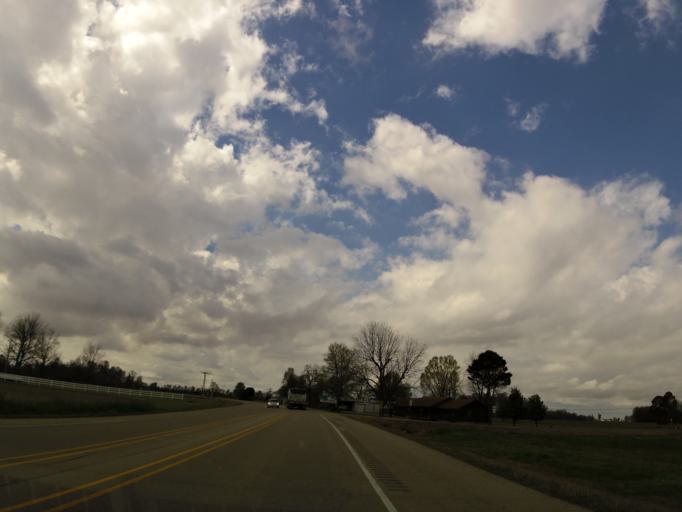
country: US
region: Arkansas
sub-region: Clay County
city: Corning
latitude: 36.4554
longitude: -90.5837
